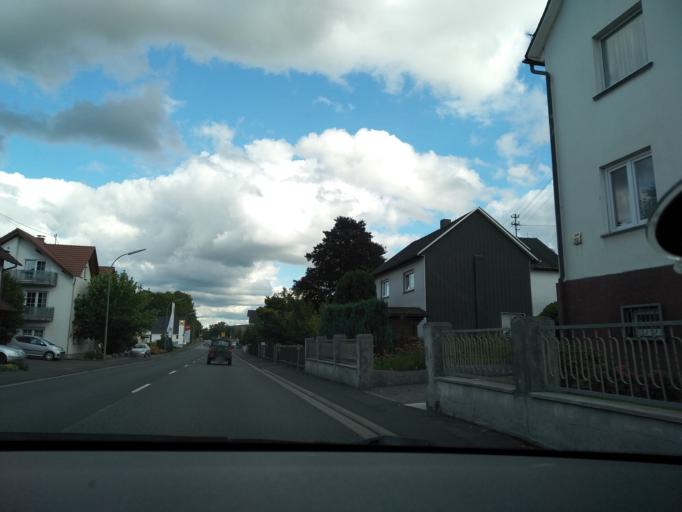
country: DE
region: Hesse
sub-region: Regierungsbezirk Giessen
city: Haiger
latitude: 50.7463
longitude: 8.1864
